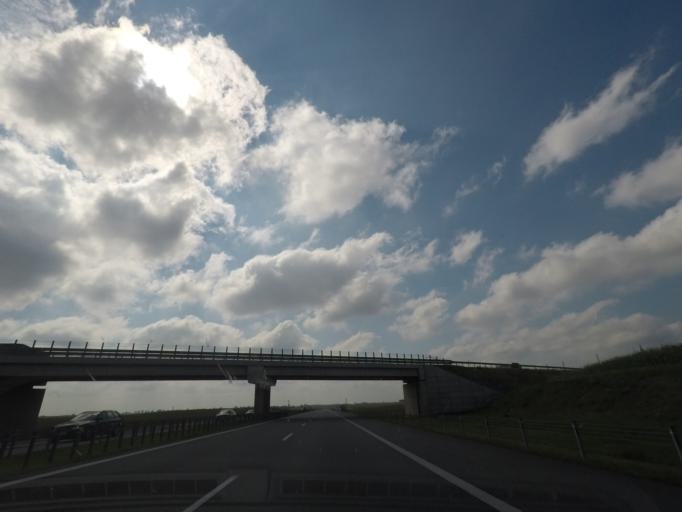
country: PL
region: Kujawsko-Pomorskie
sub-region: Powiat chelminski
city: Lisewo
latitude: 53.2219
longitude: 18.7319
